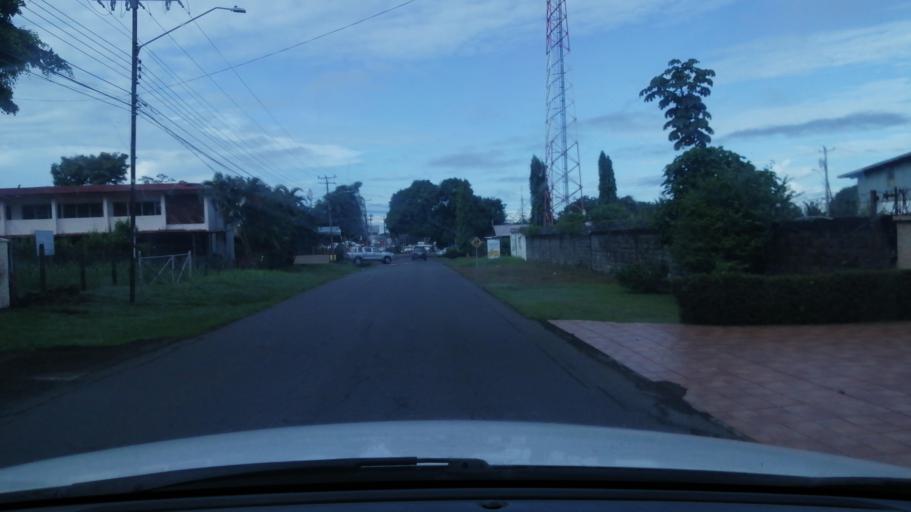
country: PA
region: Chiriqui
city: Mata del Nance
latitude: 8.4486
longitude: -82.4205
